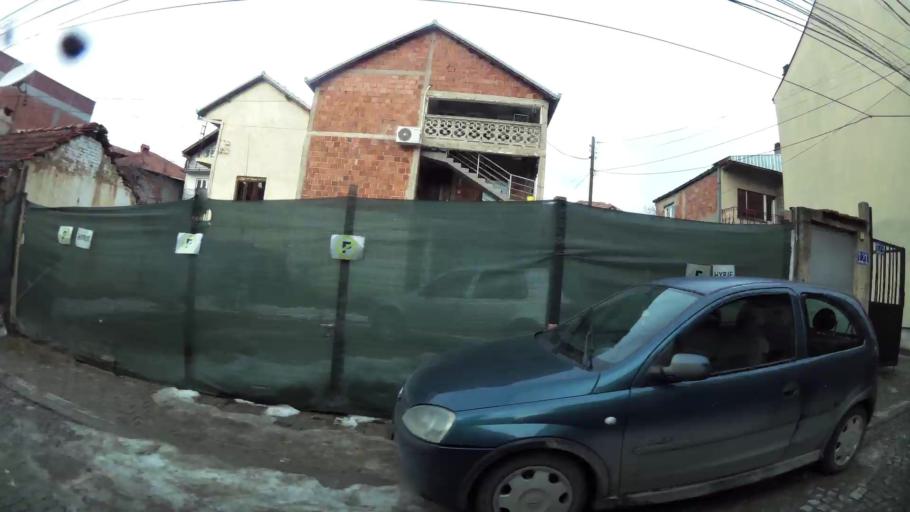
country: XK
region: Pristina
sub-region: Komuna e Prishtines
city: Pristina
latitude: 42.6693
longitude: 21.1689
